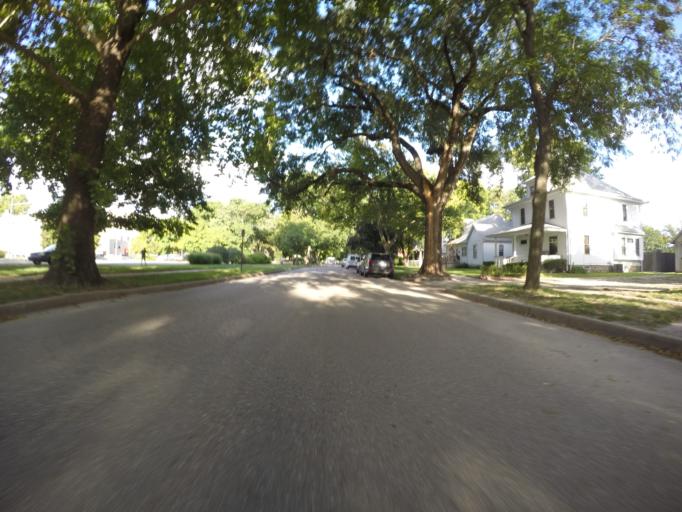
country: US
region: Kansas
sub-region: Riley County
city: Manhattan
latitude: 39.1805
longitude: -96.5698
